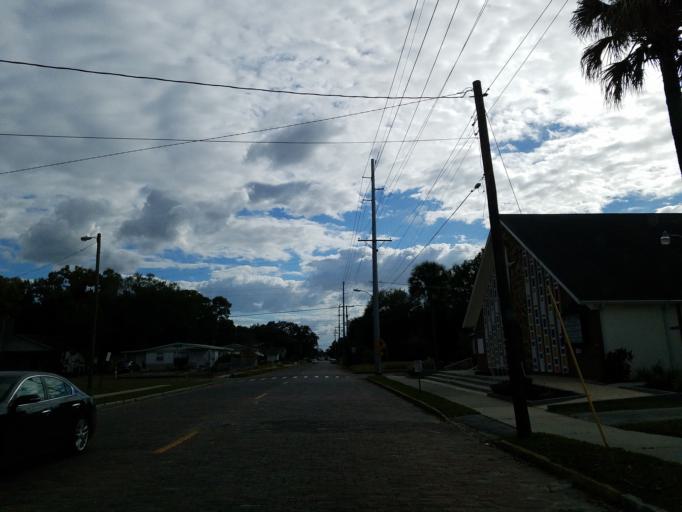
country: US
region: Florida
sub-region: Hillsborough County
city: Tampa
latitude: 27.9547
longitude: -82.4726
